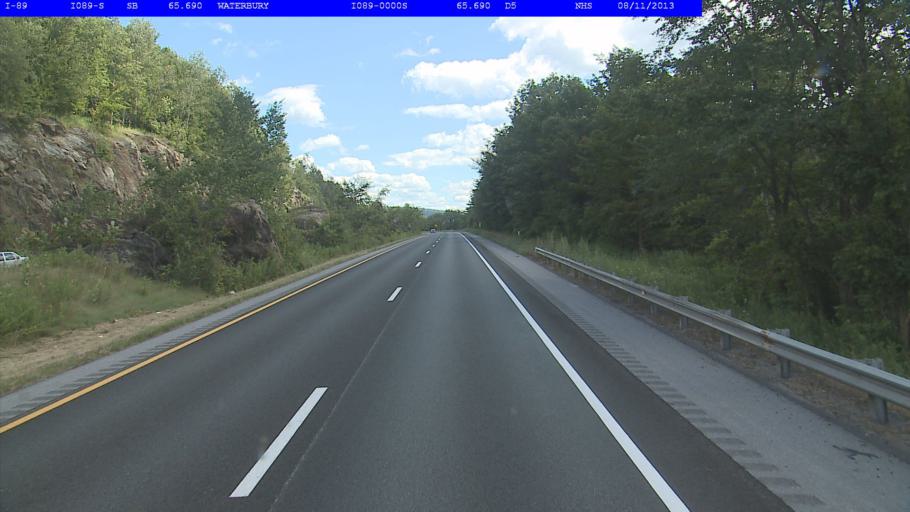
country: US
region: Vermont
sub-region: Washington County
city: Waterbury
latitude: 44.3547
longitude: -72.7864
